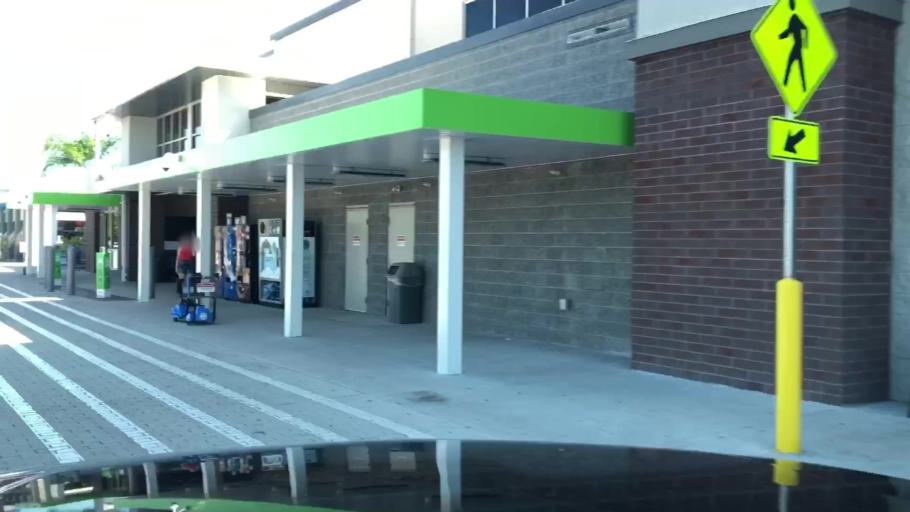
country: US
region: Florida
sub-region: Polk County
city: Citrus Ridge
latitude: 28.3301
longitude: -81.5882
